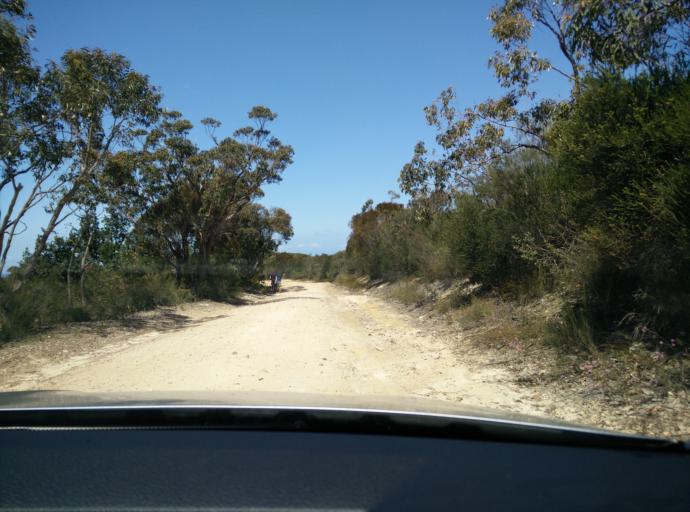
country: AU
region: New South Wales
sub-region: Gosford Shire
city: Umina
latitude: -33.5450
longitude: 151.2843
